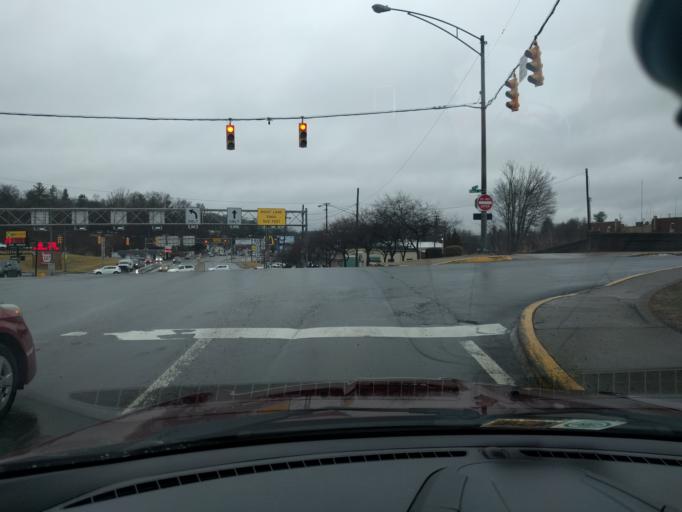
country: US
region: West Virginia
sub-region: Raleigh County
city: Beckley
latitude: 37.7754
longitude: -81.1945
